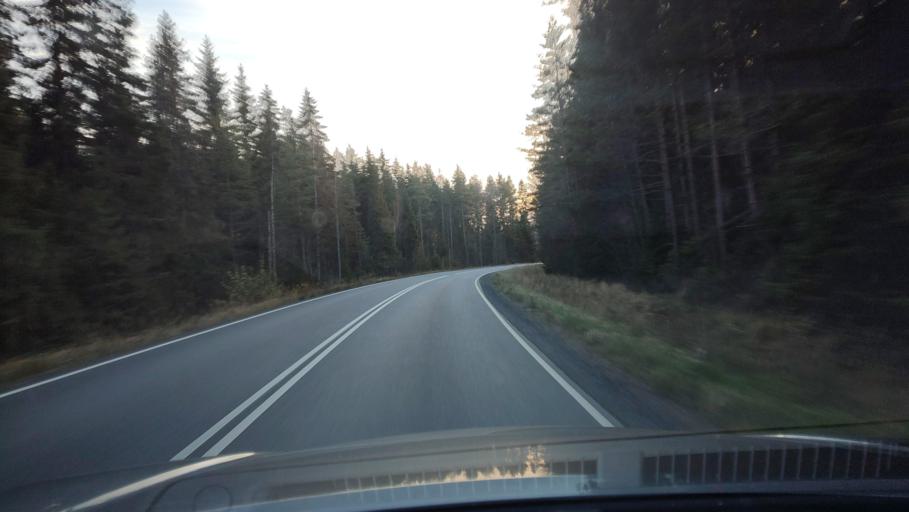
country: FI
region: Southern Ostrobothnia
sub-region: Suupohja
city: Karijoki
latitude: 62.2730
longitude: 21.5655
